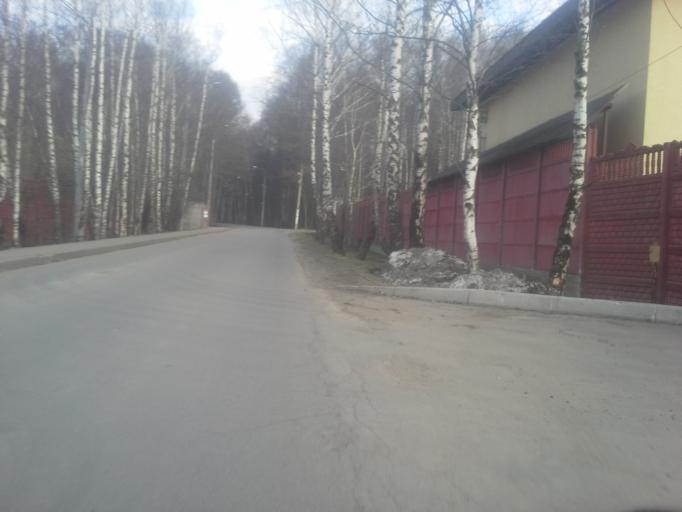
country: RU
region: Moskovskaya
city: Odintsovo
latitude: 55.6421
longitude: 37.2708
